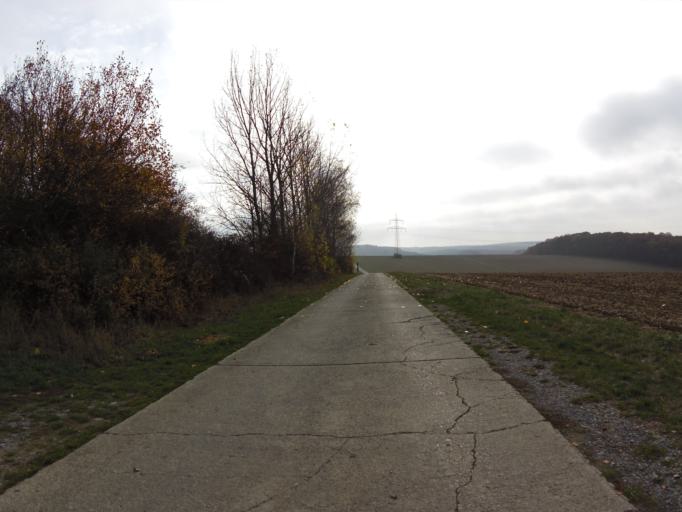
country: DE
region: Bavaria
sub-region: Regierungsbezirk Unterfranken
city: Eisingen
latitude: 49.7590
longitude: 9.8177
